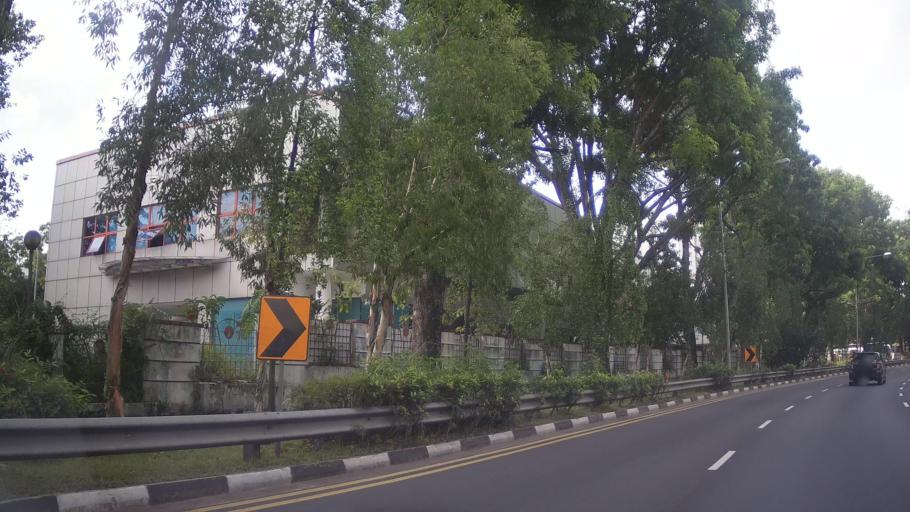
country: MY
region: Johor
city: Johor Bahru
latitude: 1.4071
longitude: 103.7467
